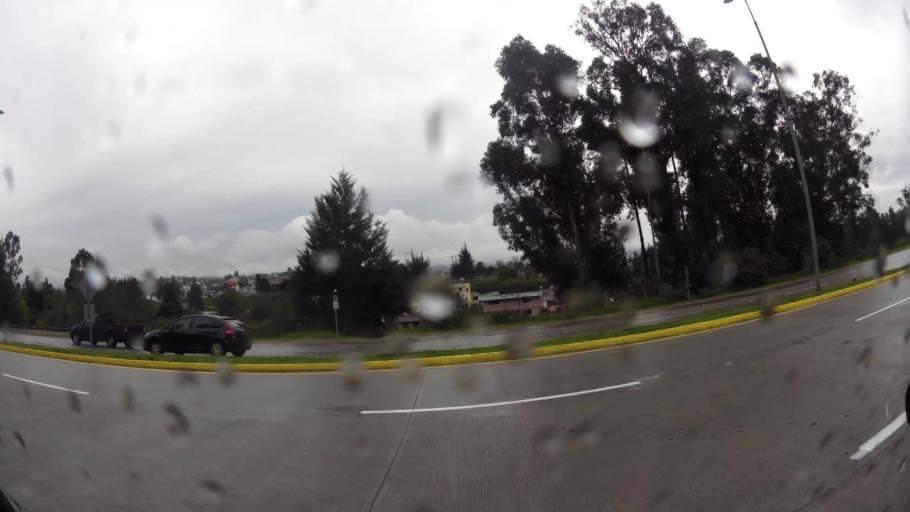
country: EC
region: Pichincha
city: Sangolqui
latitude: -0.2885
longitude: -78.4608
